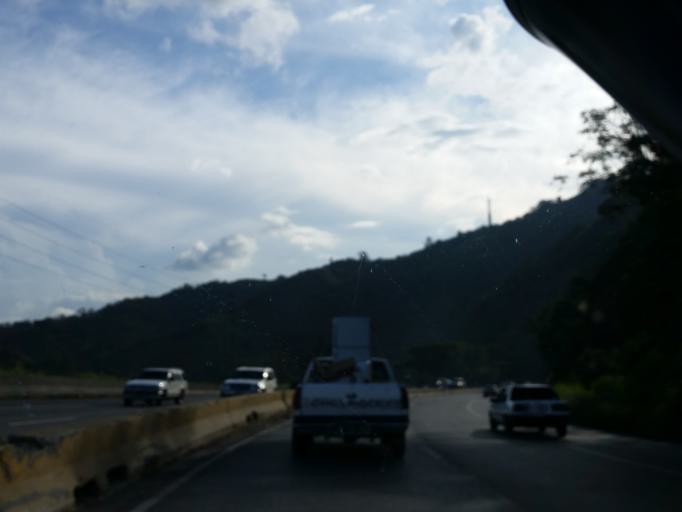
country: VE
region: Miranda
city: Caucaguita
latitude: 10.3208
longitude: -66.8733
